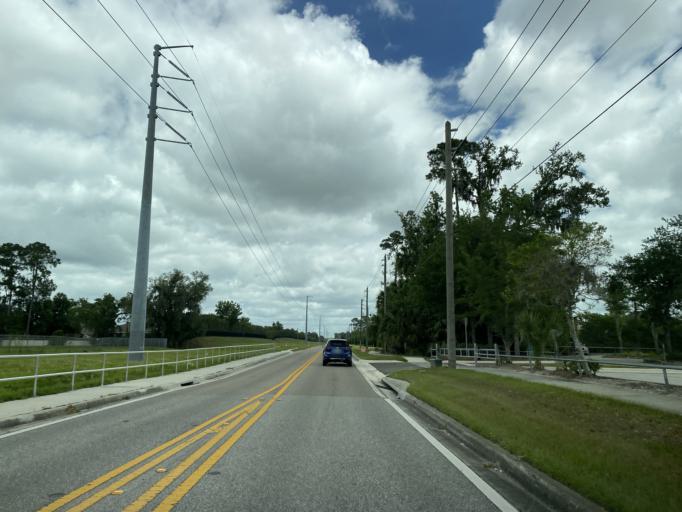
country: US
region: Florida
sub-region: Seminole County
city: Lake Mary
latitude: 28.8166
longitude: -81.3392
